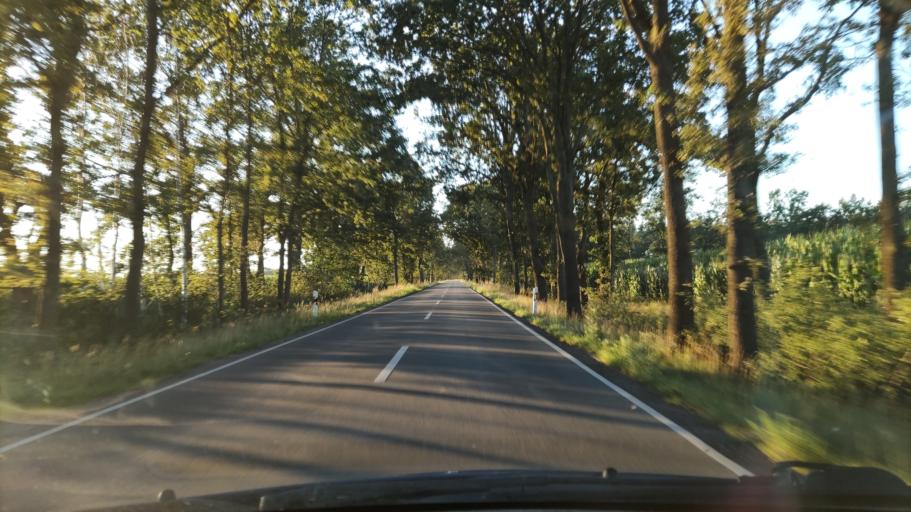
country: DE
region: Lower Saxony
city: Klein Gusborn
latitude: 53.0413
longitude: 11.1781
